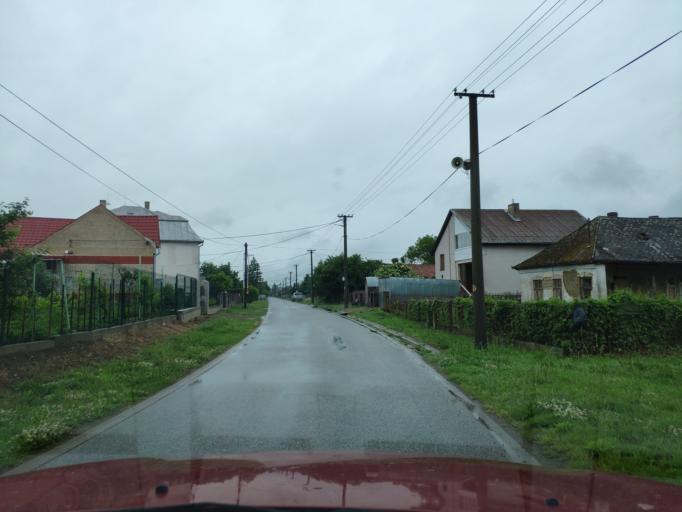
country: SK
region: Kosicky
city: Cierna nad Tisou
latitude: 48.4108
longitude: 22.0585
